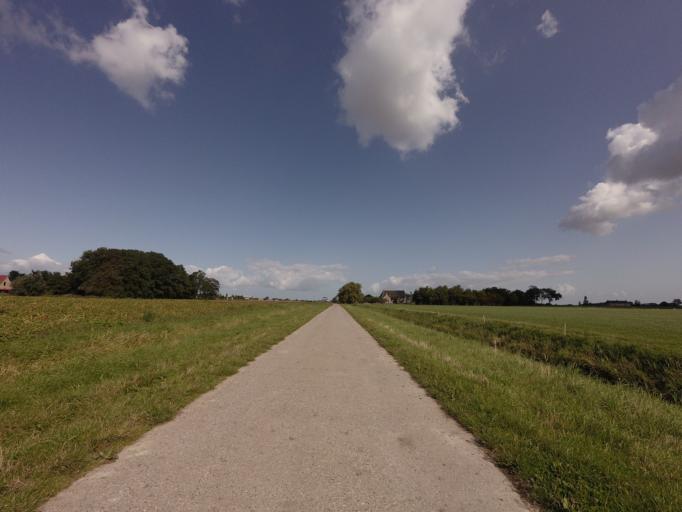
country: NL
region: Friesland
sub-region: Gemeente Het Bildt
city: Sint Jacobiparochie
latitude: 53.2715
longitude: 5.6156
